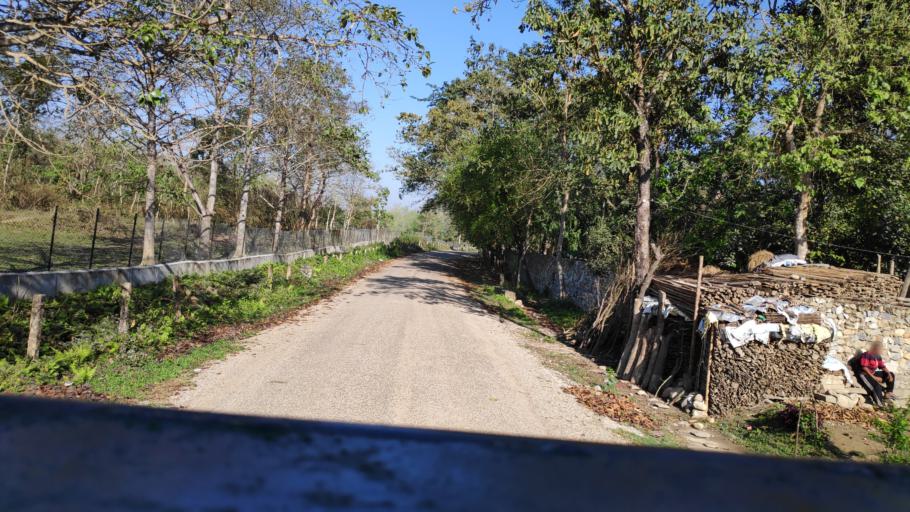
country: NP
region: Central Region
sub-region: Narayani Zone
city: Bharatpur
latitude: 27.5676
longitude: 84.5205
